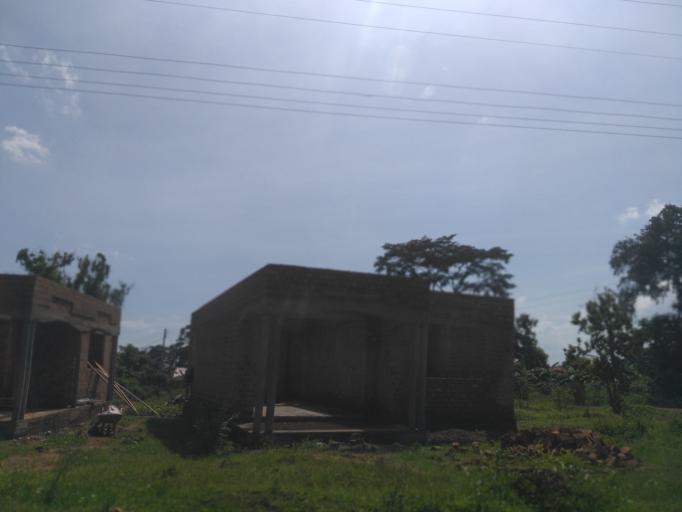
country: UG
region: Central Region
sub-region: Wakiso District
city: Kireka
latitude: 0.4524
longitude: 32.5826
